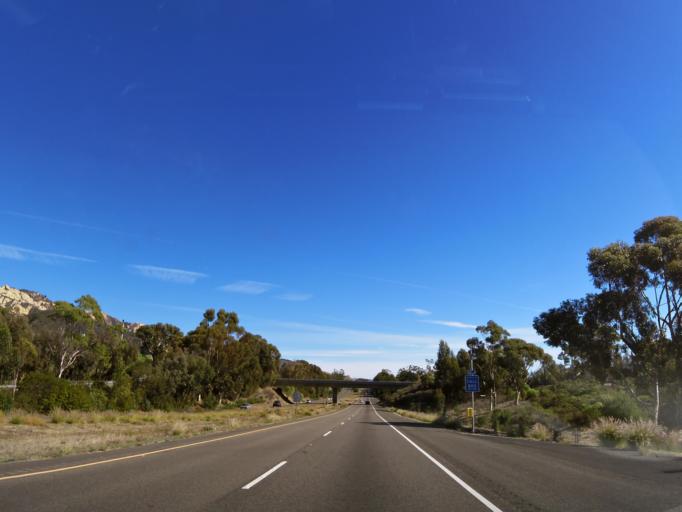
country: US
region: California
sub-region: Santa Barbara County
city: Buellton
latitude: 34.4734
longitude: -120.2092
